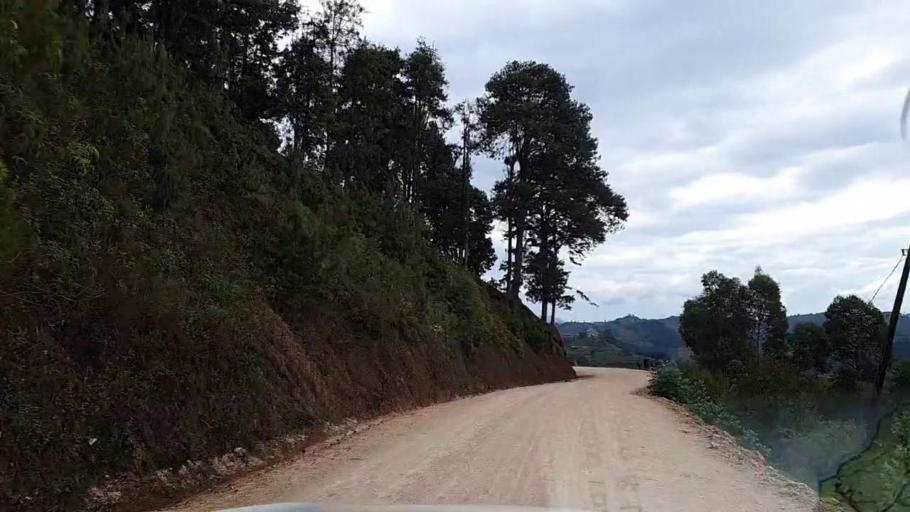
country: RW
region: Southern Province
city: Nzega
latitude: -2.4056
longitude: 29.4542
